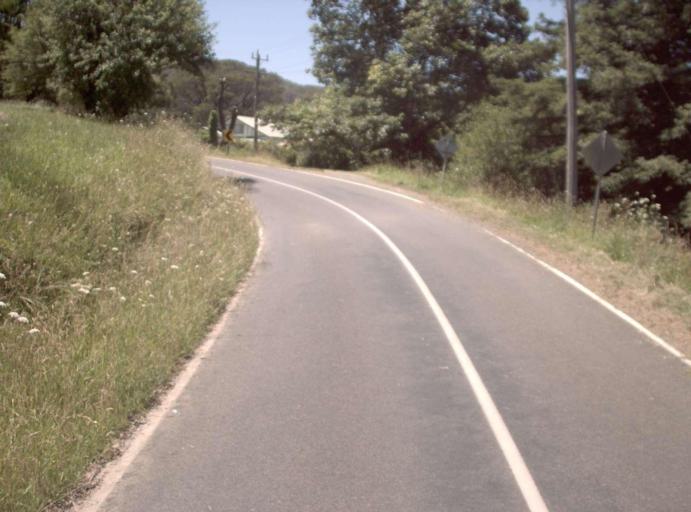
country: AU
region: Victoria
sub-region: Yarra Ranges
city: Millgrove
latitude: -37.7509
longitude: 145.7082
